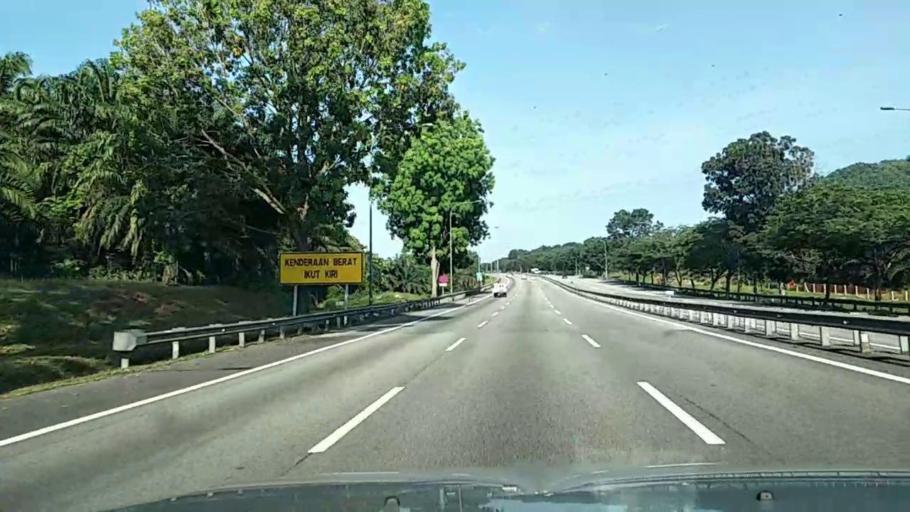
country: MY
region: Negeri Sembilan
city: Kampung Baharu Nilai
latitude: 2.8530
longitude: 101.7315
